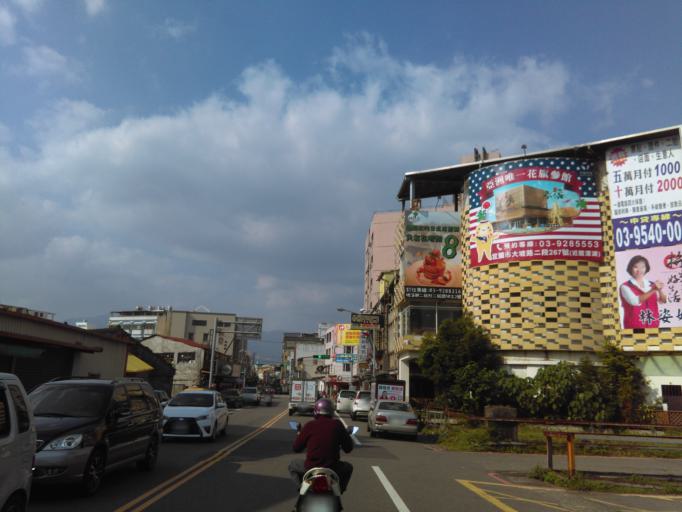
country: TW
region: Taiwan
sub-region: Yilan
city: Yilan
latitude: 24.7582
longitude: 121.7588
